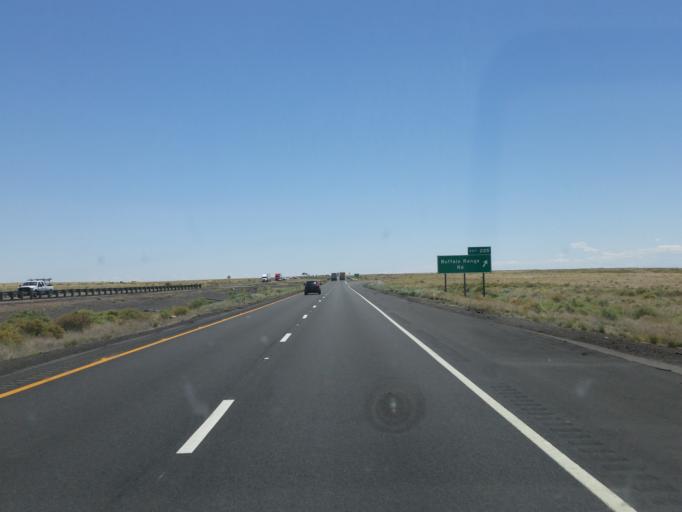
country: US
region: Arizona
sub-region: Coconino County
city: LeChee
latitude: 35.1311
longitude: -111.1898
